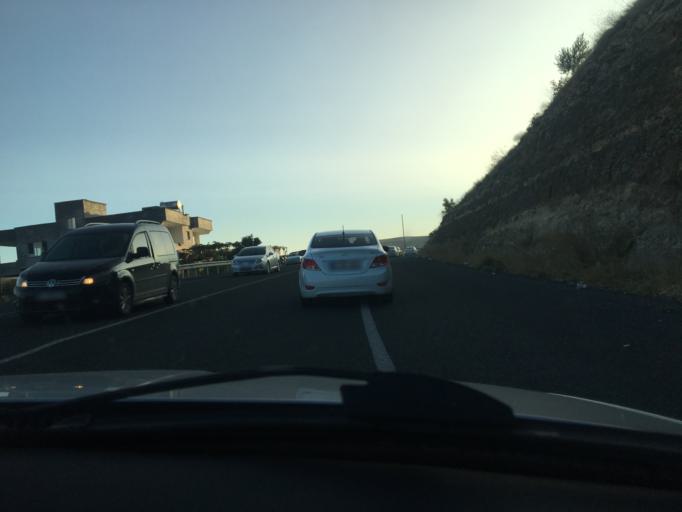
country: TR
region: Sanliurfa
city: Halfeti
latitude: 37.2043
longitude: 37.9708
